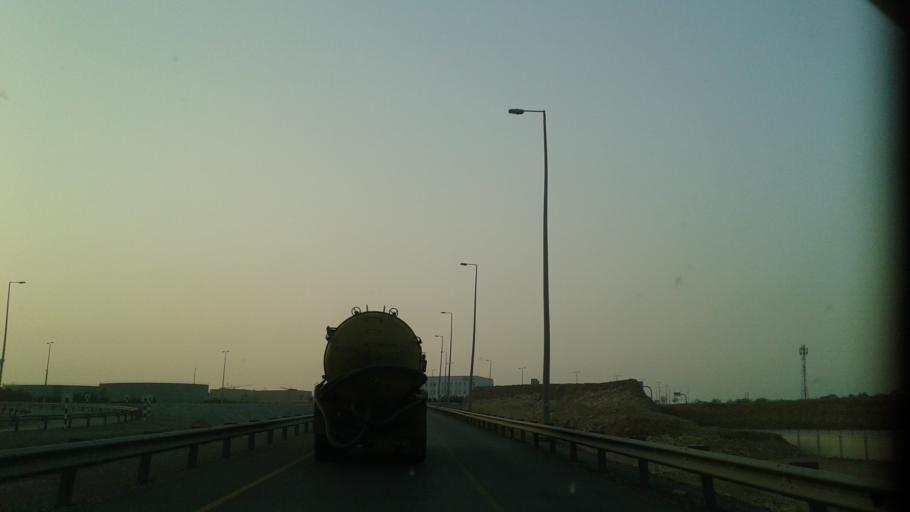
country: OM
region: Muhafazat Masqat
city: Bawshar
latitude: 23.5627
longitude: 58.3408
